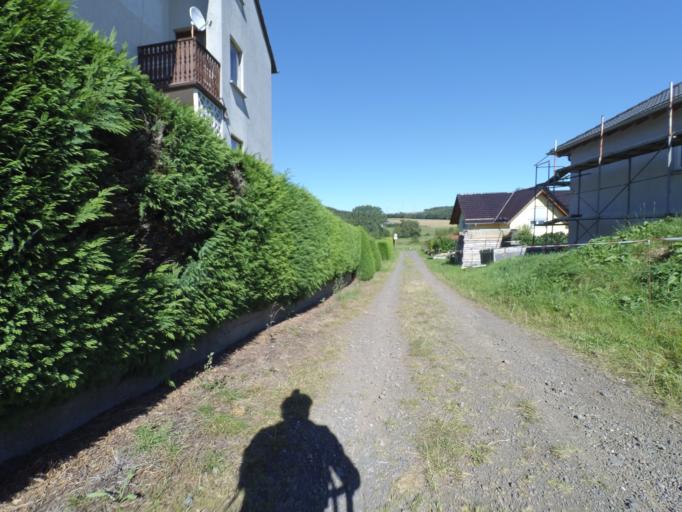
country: DE
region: Rheinland-Pfalz
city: Oberstadtfeld
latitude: 50.2085
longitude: 6.7922
